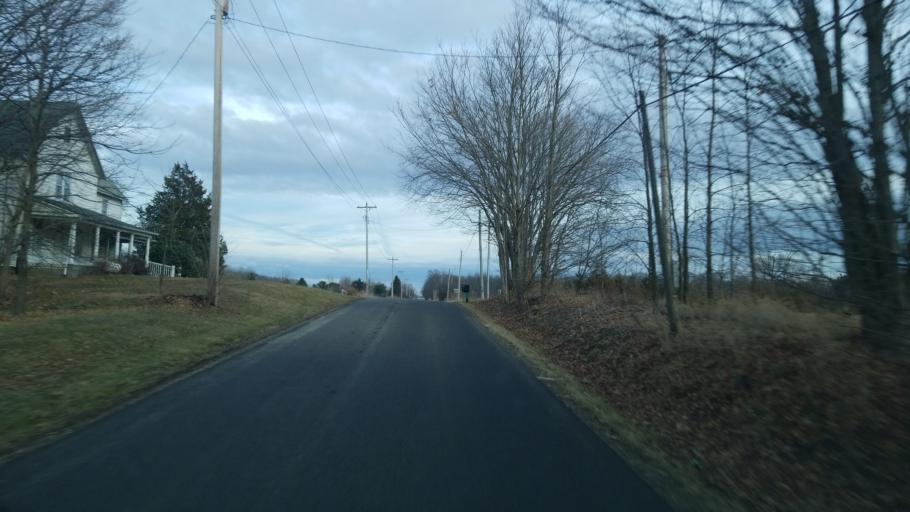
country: US
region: Ohio
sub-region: Morrow County
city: Mount Gilead
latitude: 40.5153
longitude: -82.7974
